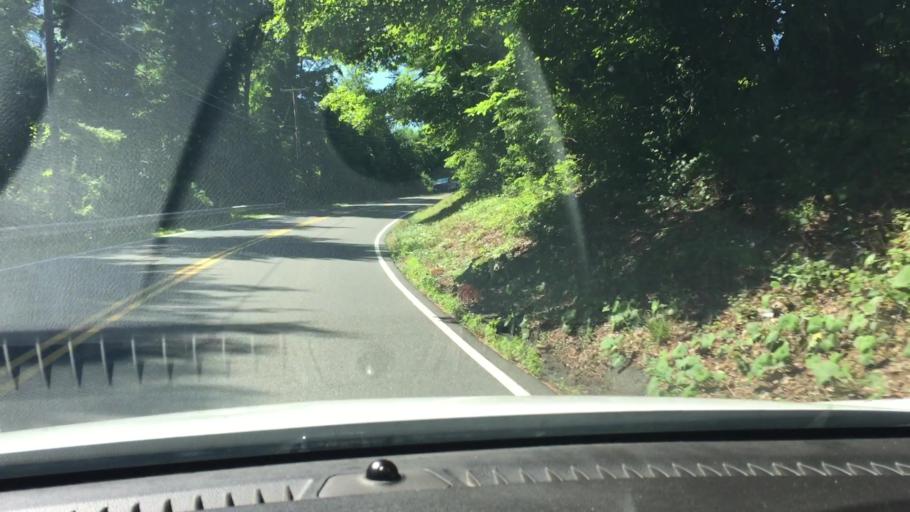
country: US
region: Massachusetts
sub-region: Berkshire County
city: Lenox
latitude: 42.3757
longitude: -73.2571
